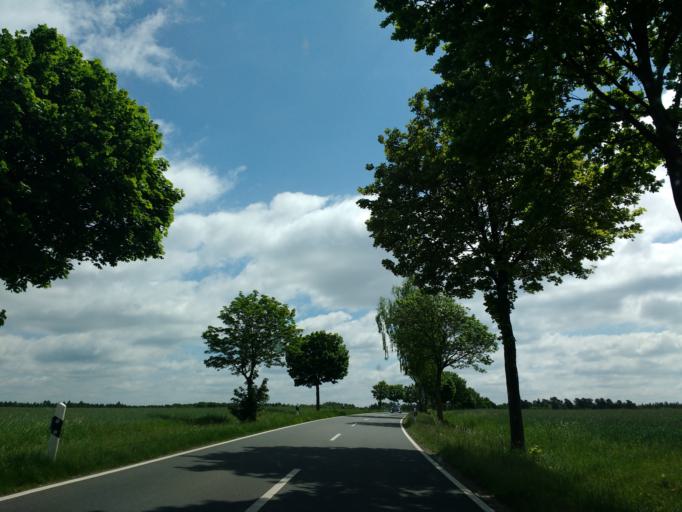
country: DE
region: Lower Saxony
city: Walsrode
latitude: 52.8488
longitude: 9.6094
